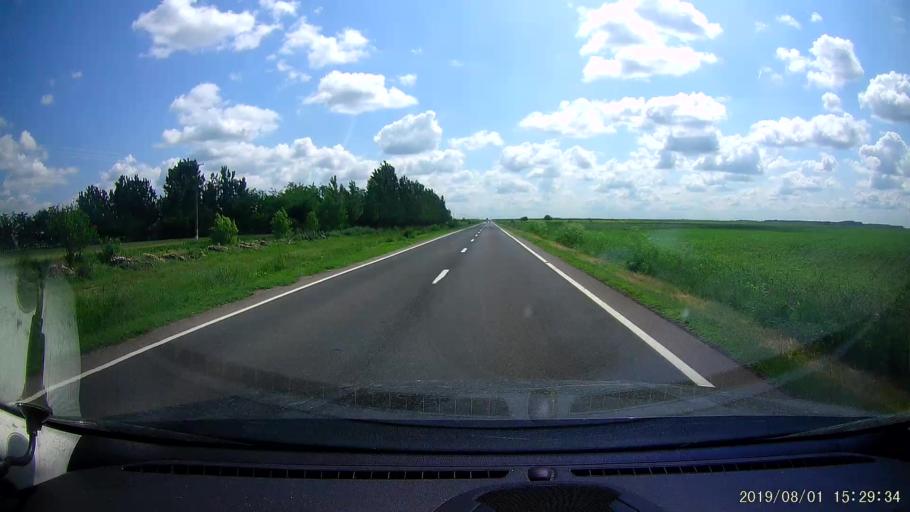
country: RO
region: Braila
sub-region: Comuna Viziru
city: Viziru
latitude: 44.9795
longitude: 27.6944
